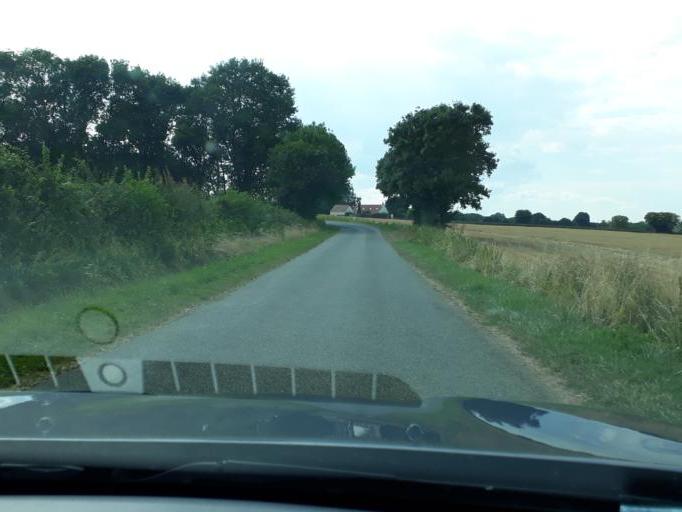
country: FR
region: Centre
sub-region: Departement du Cher
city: Nerondes
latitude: 47.0415
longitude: 2.8945
